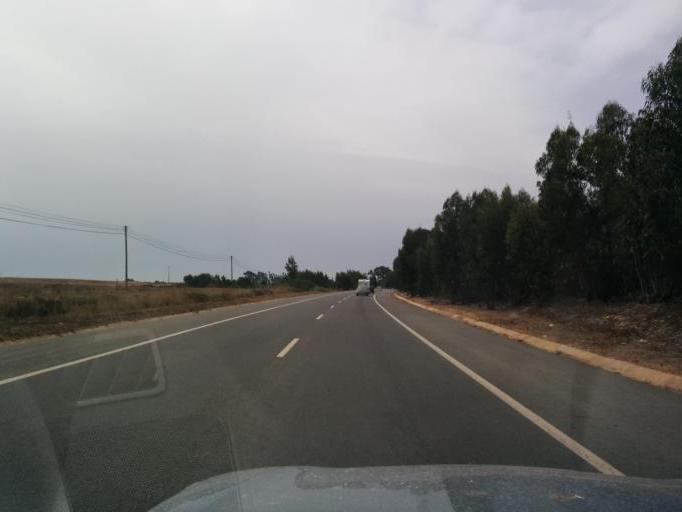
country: PT
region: Beja
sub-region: Odemira
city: Vila Nova de Milfontes
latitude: 37.7138
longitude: -8.7667
